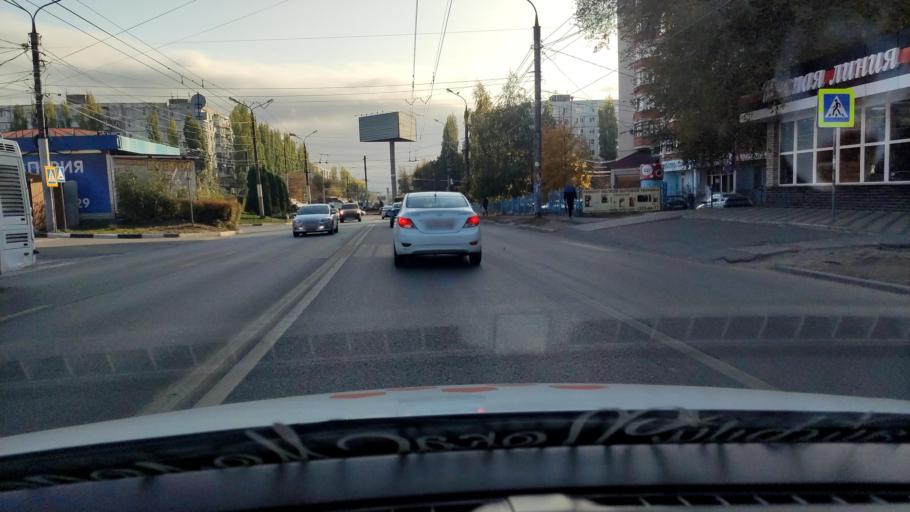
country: RU
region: Voronezj
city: Podgornoye
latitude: 51.7068
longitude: 39.1479
